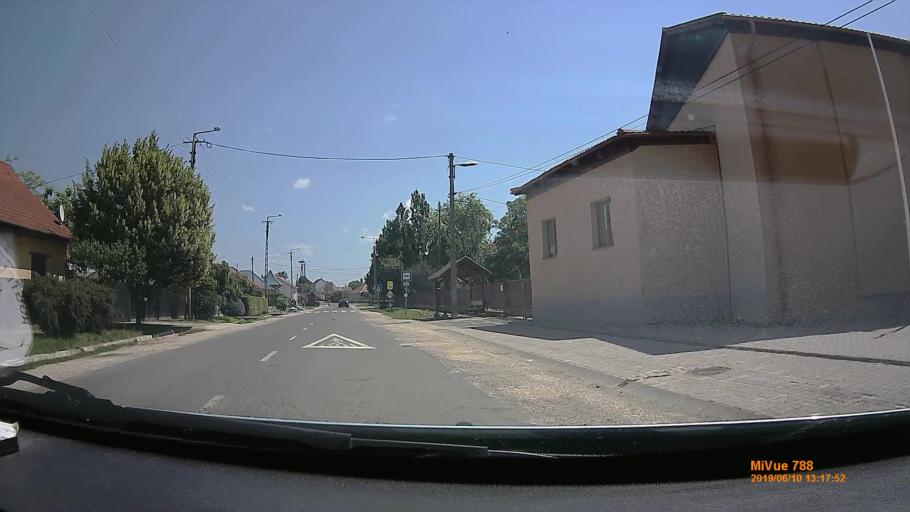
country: HU
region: Borsod-Abauj-Zemplen
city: Tiszaluc
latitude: 48.0366
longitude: 21.0635
